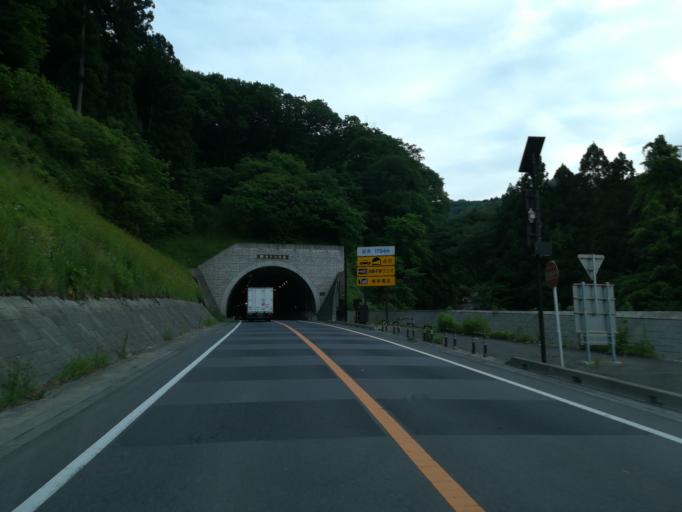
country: JP
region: Ibaraki
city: Tsukuba
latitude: 36.1819
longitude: 140.1667
